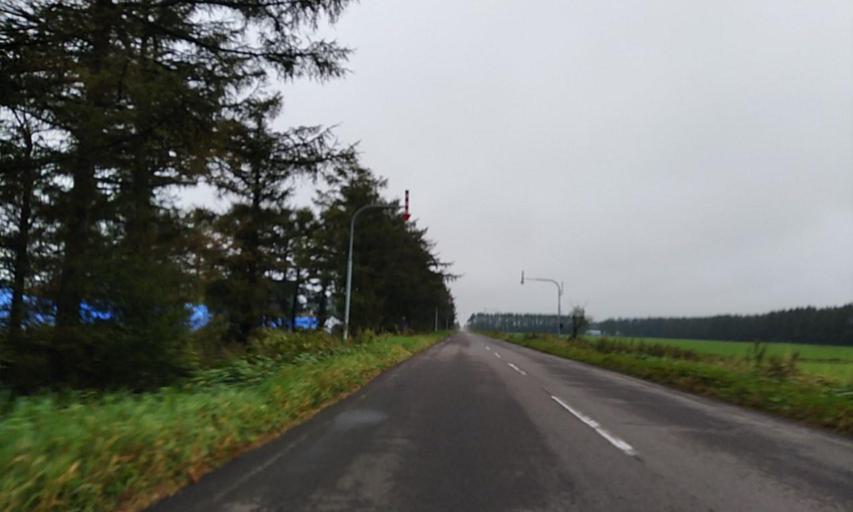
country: JP
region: Hokkaido
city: Shibetsu
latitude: 43.5169
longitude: 144.6799
